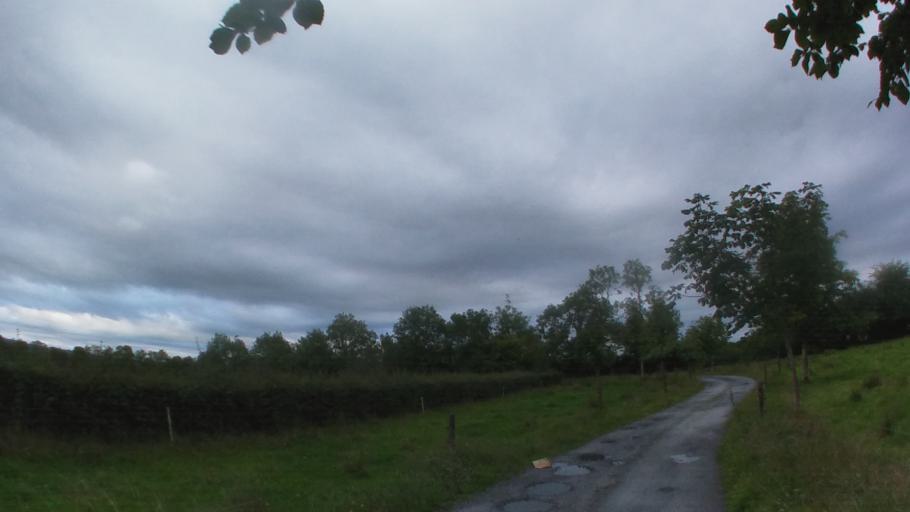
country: IE
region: Leinster
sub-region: Kilkenny
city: Kilkenny
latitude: 52.6780
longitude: -7.2225
